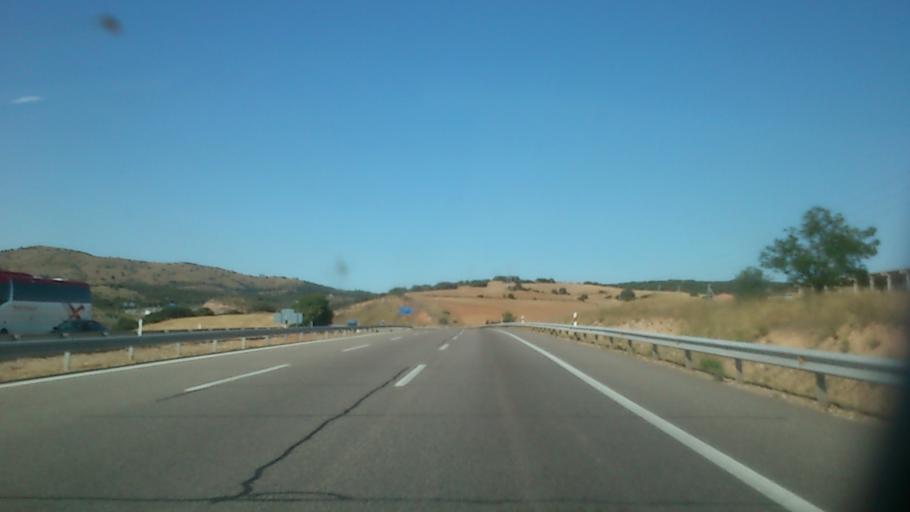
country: ES
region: Aragon
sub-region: Provincia de Zaragoza
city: Sediles
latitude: 41.3719
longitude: -1.5750
